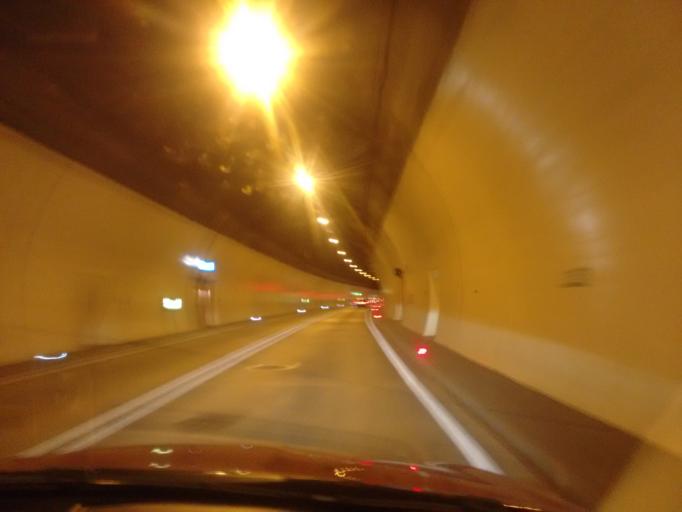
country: AT
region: Upper Austria
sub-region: Politischer Bezirk Gmunden
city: Ebensee
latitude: 47.8462
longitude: 13.7799
